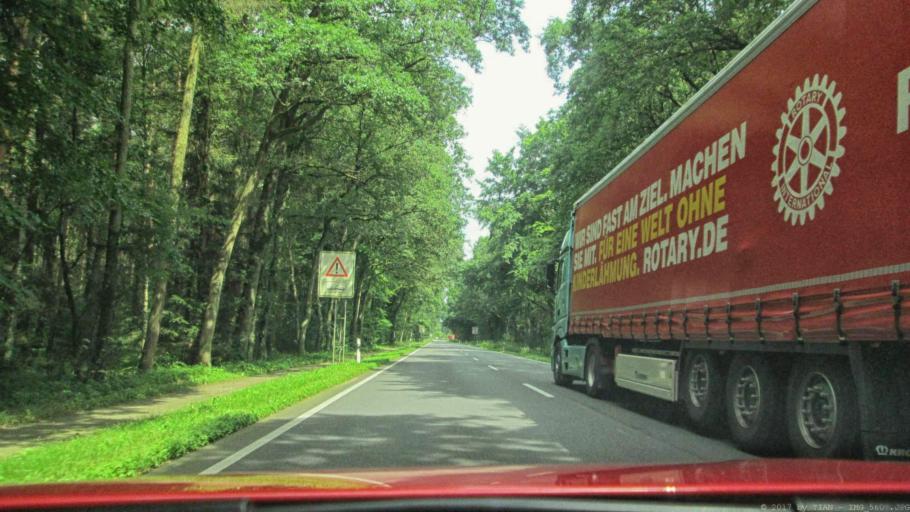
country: DE
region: Lower Saxony
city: Suderburg
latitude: 52.8843
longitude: 10.5039
